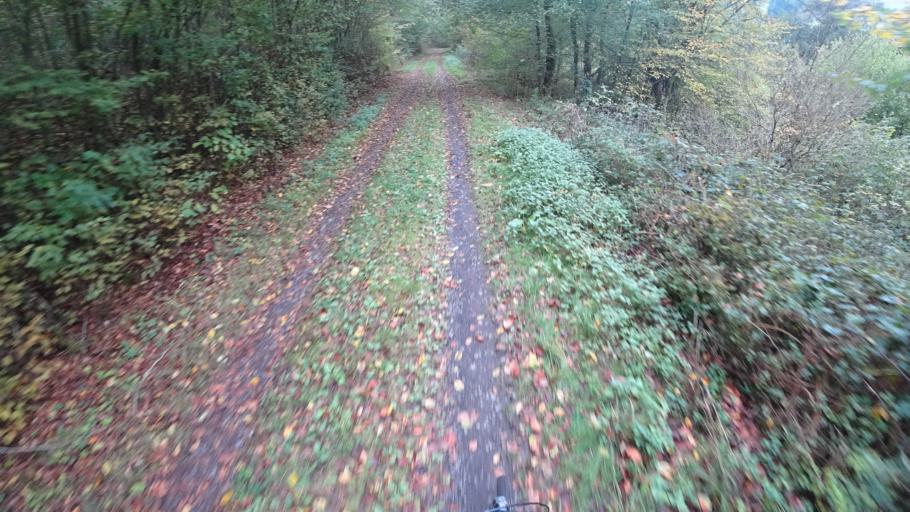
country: DE
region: Rheinland-Pfalz
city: Isselbach
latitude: 50.3997
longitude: 7.8981
